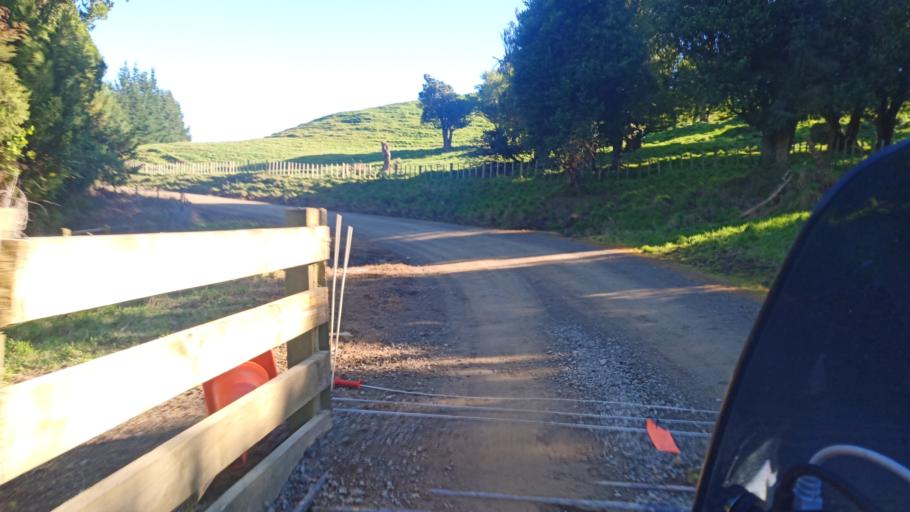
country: NZ
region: Hawke's Bay
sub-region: Wairoa District
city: Wairoa
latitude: -38.7933
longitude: 177.2800
